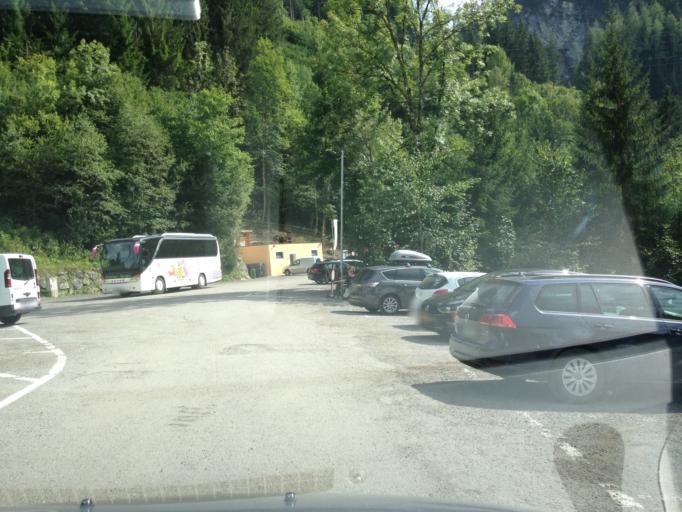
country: AT
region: Salzburg
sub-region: Politischer Bezirk Zell am See
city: Taxenbach
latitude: 47.2895
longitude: 12.9759
